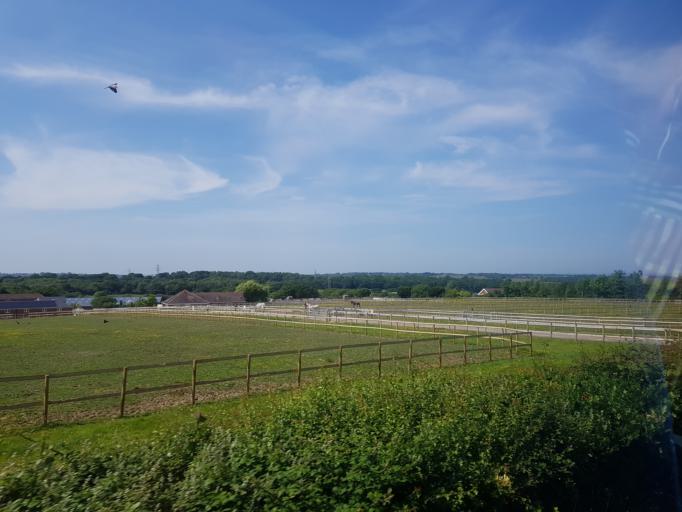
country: GB
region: England
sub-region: Isle of Wight
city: Newport
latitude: 50.7076
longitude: -1.2599
